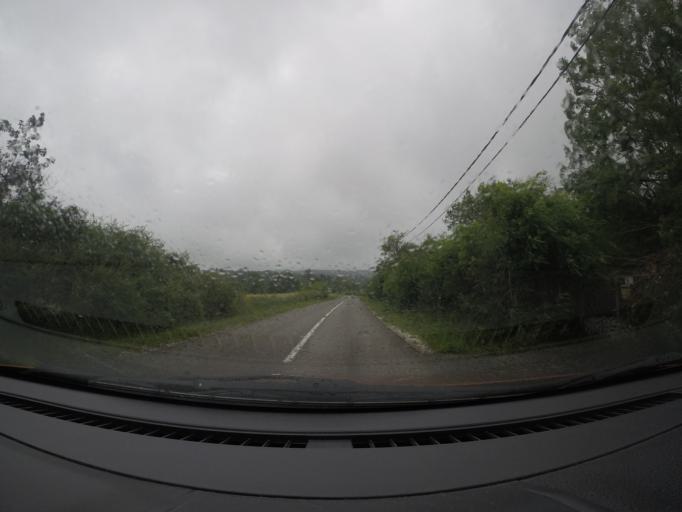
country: RS
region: Central Serbia
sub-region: Belgrade
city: Sopot
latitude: 44.5215
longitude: 20.5351
